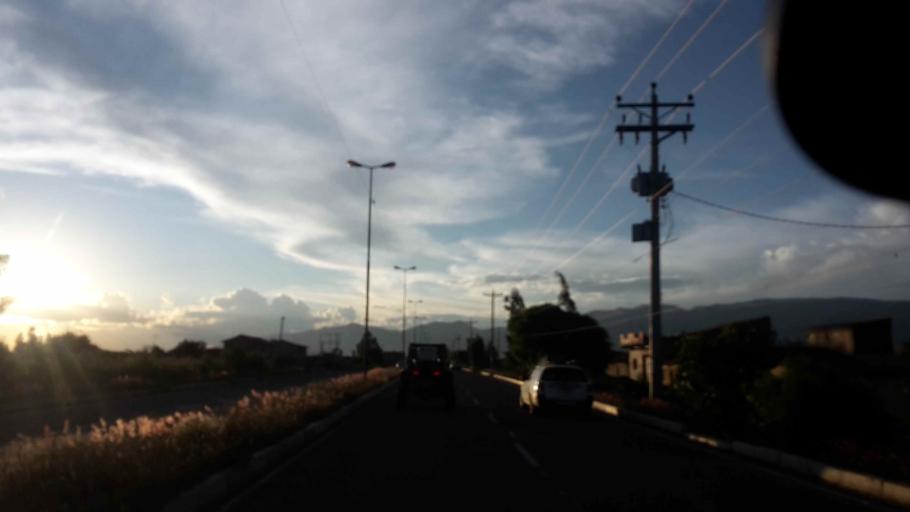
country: BO
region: Cochabamba
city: Punata
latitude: -17.5546
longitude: -65.8137
